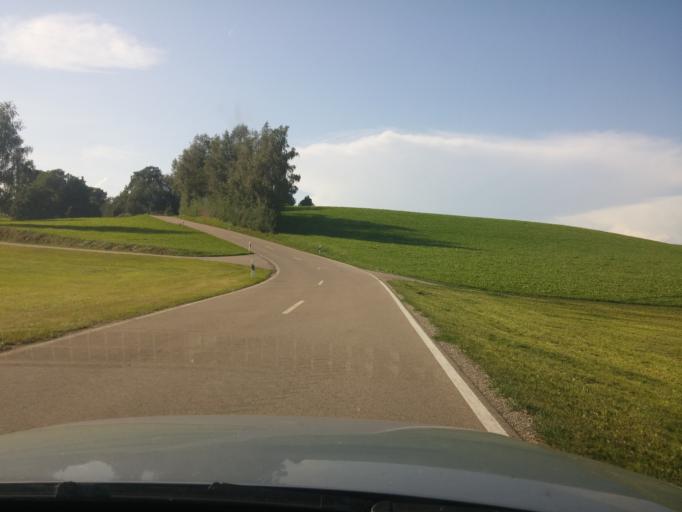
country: DE
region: Bavaria
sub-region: Swabia
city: Legau
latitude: 47.8427
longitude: 10.0901
